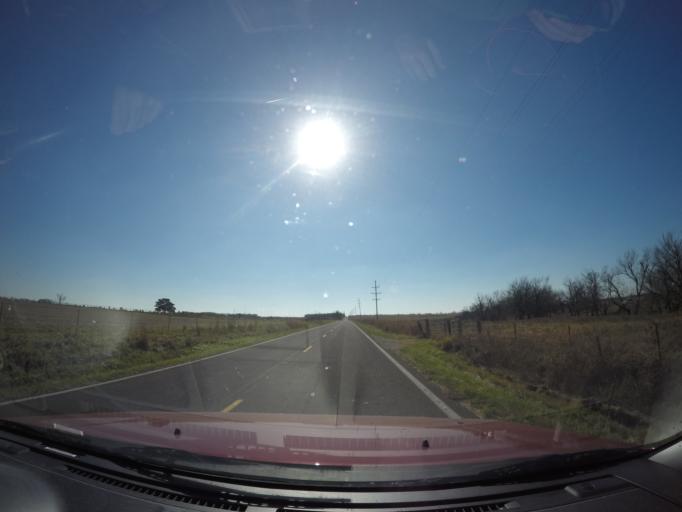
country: US
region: Kansas
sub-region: Morris County
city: Council Grove
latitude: 38.8651
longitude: -96.5939
